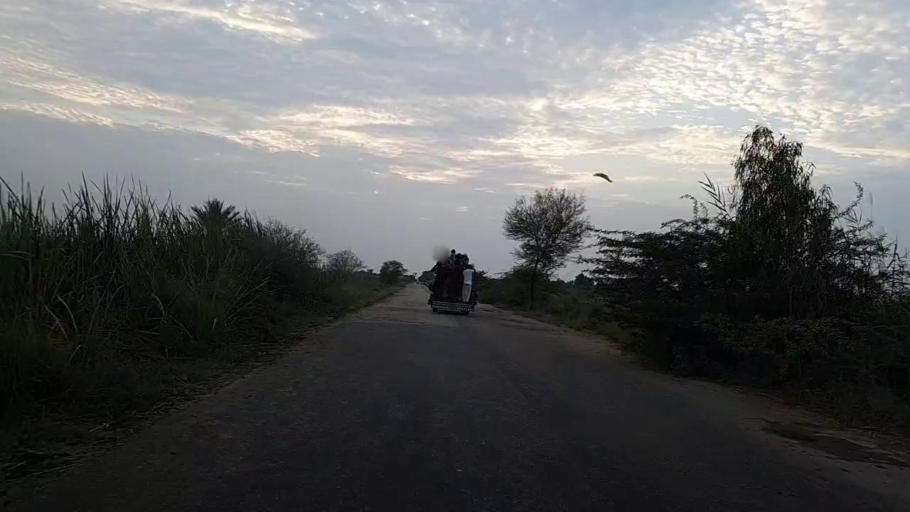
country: PK
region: Sindh
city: Naushahro Firoz
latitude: 26.8156
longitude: 68.1826
